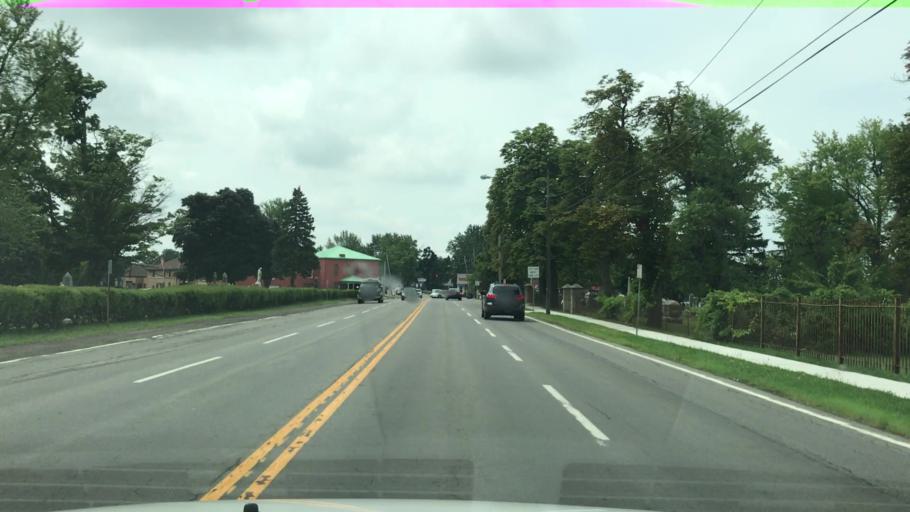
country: US
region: New York
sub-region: Erie County
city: Sloan
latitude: 42.9217
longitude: -78.7928
